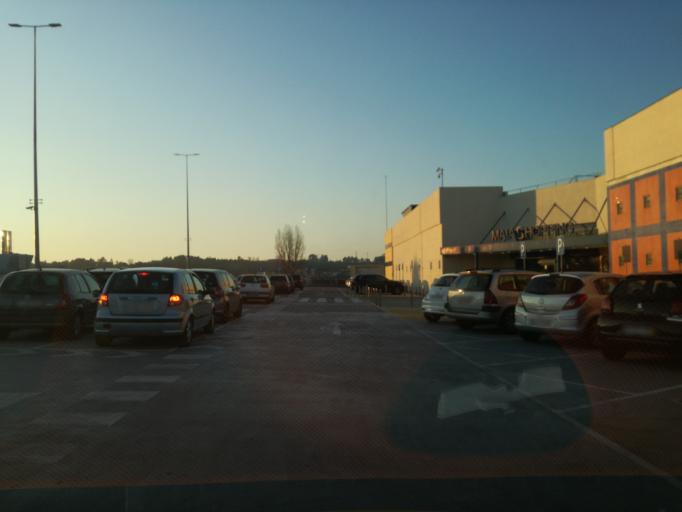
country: PT
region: Porto
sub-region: Valongo
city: Ermesinde
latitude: 41.2200
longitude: -8.5624
